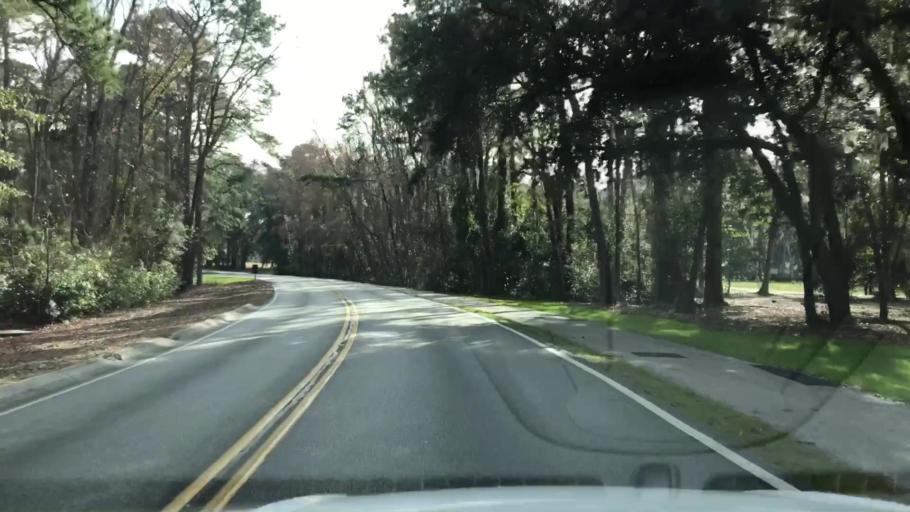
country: US
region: South Carolina
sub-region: Beaufort County
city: Hilton Head Island
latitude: 32.2207
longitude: -80.7237
